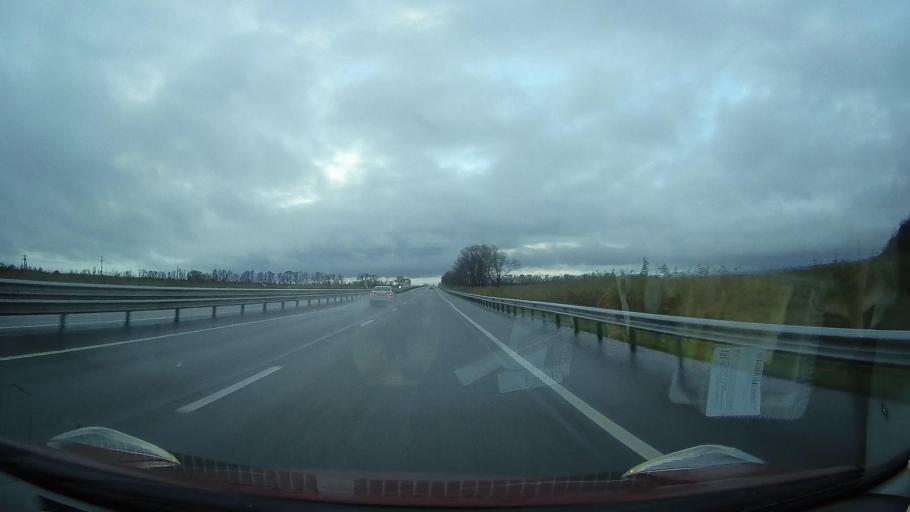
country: RU
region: Stavropol'skiy
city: Zavetnoye
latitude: 44.7861
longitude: 41.5153
